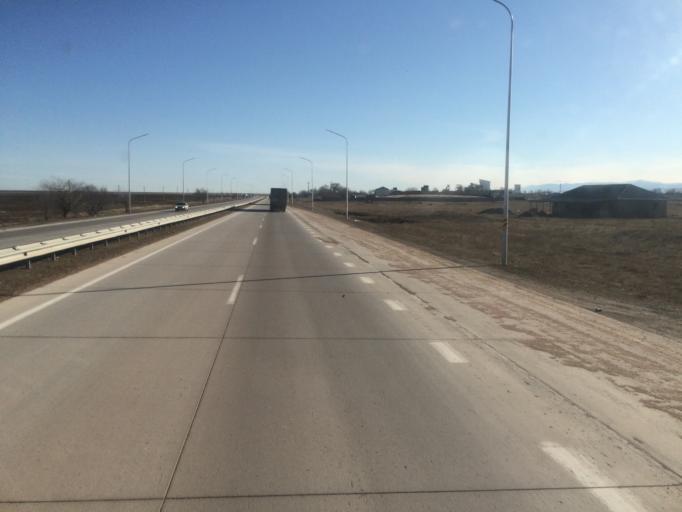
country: KZ
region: Zhambyl
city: Kulan
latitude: 42.9929
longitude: 72.3121
